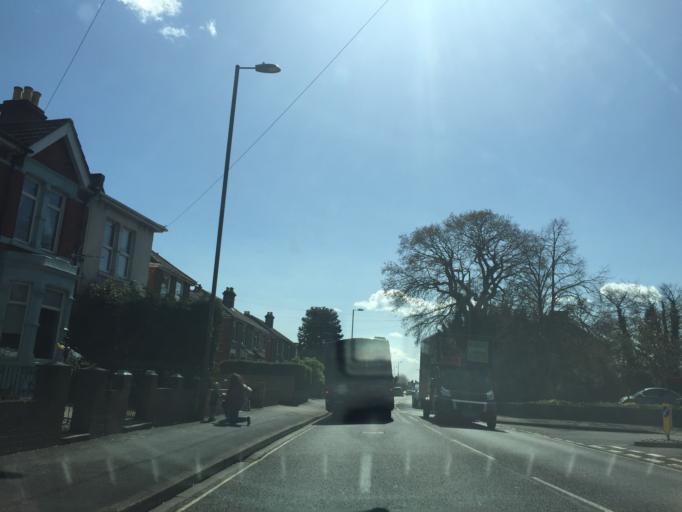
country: GB
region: England
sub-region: Hampshire
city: Gosport
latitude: 50.8101
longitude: -1.1534
